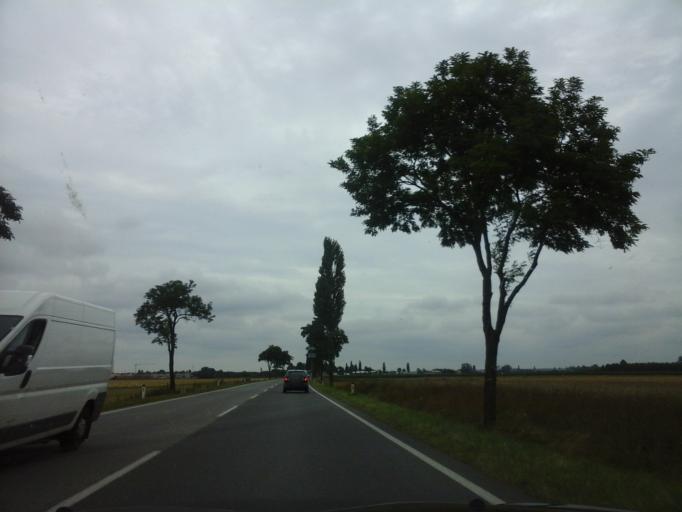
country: AT
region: Lower Austria
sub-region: Politischer Bezirk Ganserndorf
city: Engelhartstetten
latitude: 48.1665
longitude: 16.8945
